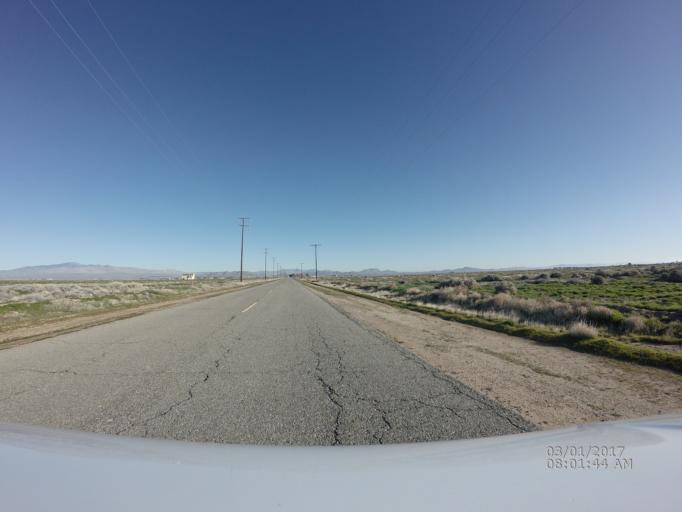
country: US
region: California
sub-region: Kern County
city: Rosamond
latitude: 34.7930
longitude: -118.2550
